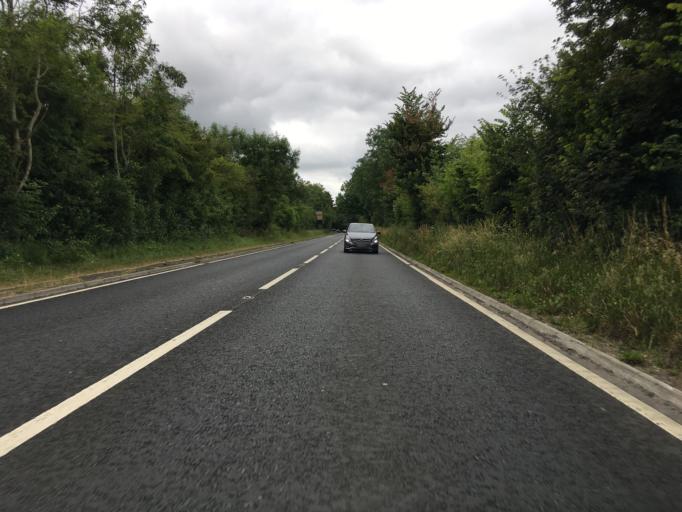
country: GB
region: England
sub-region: Gloucestershire
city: Shipton Village
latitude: 51.8817
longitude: -1.9782
